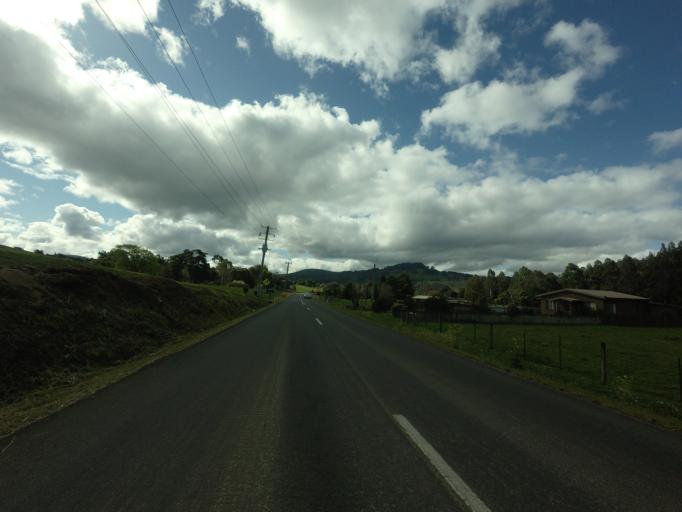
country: AU
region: Tasmania
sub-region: Huon Valley
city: Geeveston
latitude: -43.1732
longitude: 146.9239
